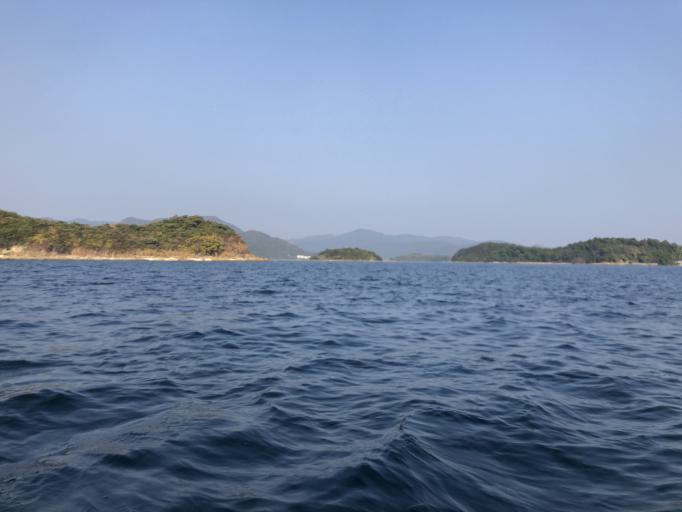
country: HK
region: Sai Kung
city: Sai Kung
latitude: 22.3718
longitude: 114.2836
